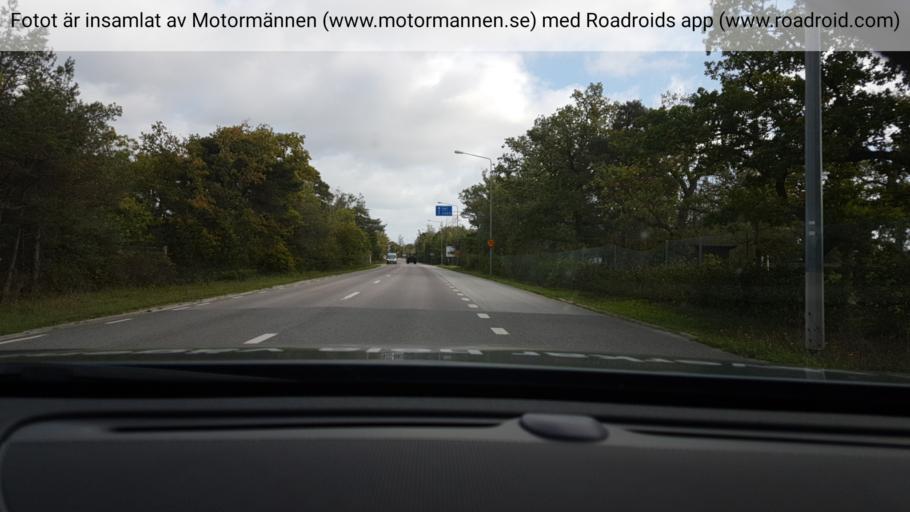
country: SE
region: Gotland
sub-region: Gotland
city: Slite
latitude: 57.8572
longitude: 19.0420
